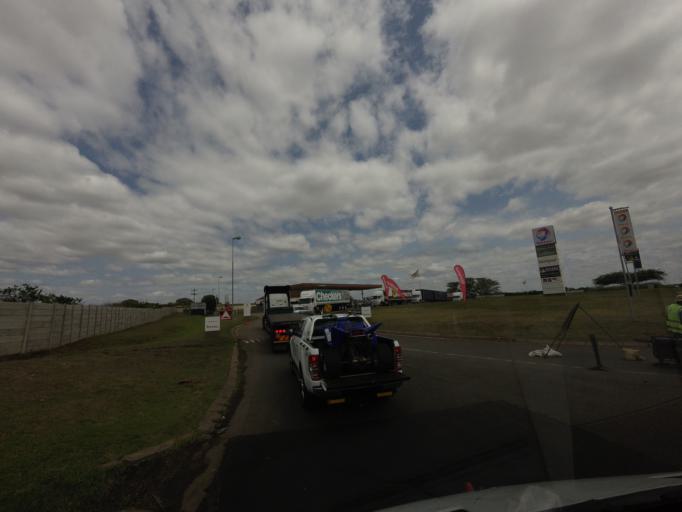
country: ZA
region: KwaZulu-Natal
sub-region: uMkhanyakude District Municipality
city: Hluhluwe
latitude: -28.0902
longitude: 32.2679
